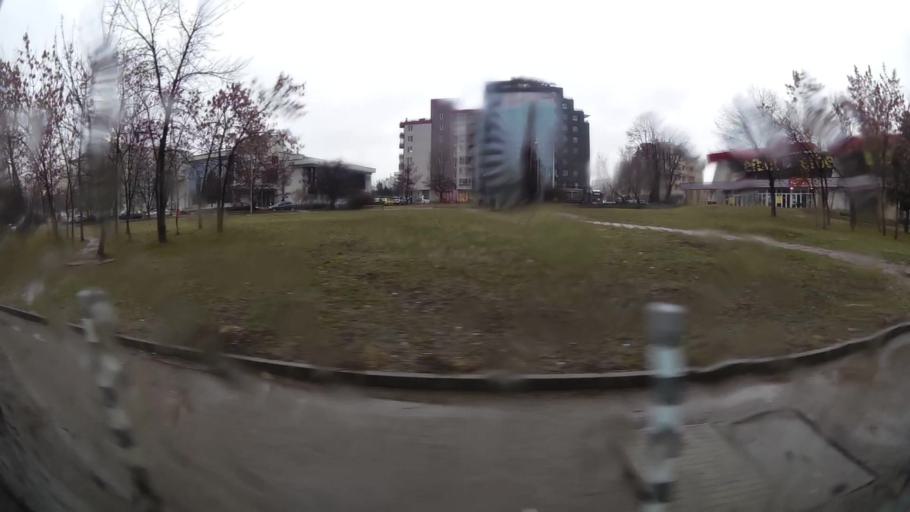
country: BG
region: Sofia-Capital
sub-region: Stolichna Obshtina
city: Sofia
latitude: 42.6518
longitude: 23.3412
